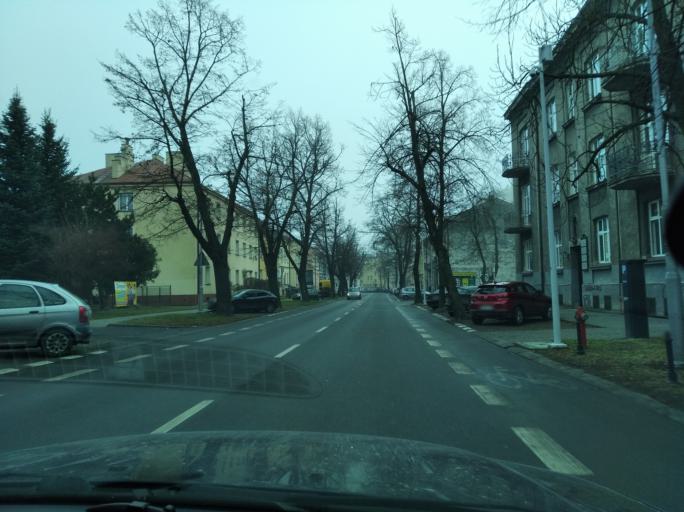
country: PL
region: Subcarpathian Voivodeship
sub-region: Rzeszow
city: Rzeszow
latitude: 50.0406
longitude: 21.9947
